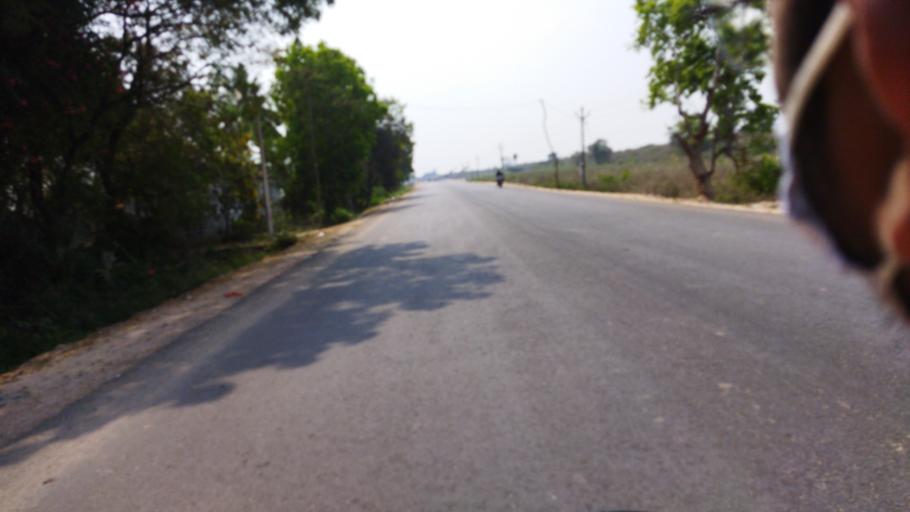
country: IN
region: Telangana
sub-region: Nalgonda
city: Nalgonda
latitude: 17.0799
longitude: 79.3215
